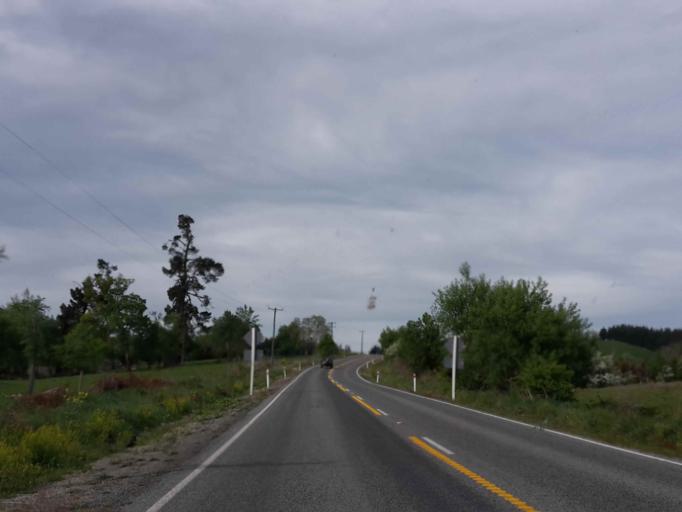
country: NZ
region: Canterbury
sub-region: Timaru District
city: Pleasant Point
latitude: -44.1282
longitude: 171.0910
